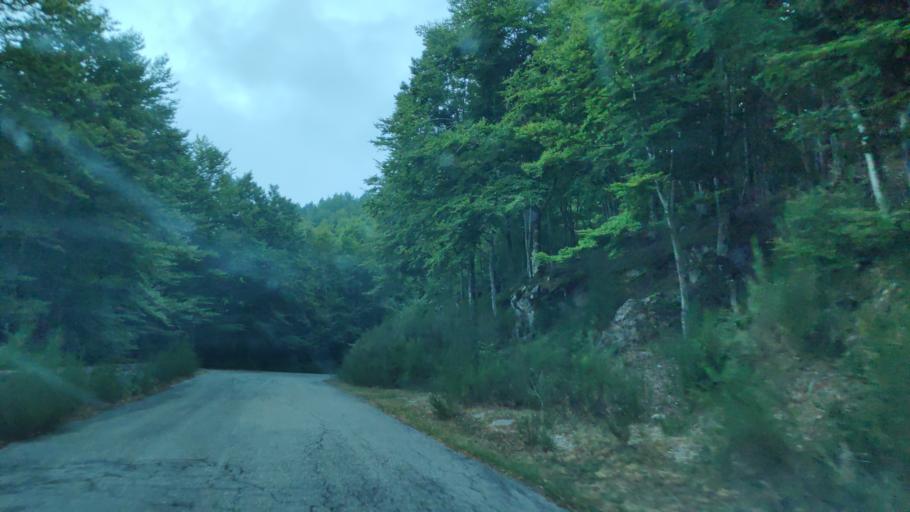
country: IT
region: Calabria
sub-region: Provincia di Vibo-Valentia
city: Nardodipace
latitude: 38.4957
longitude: 16.3541
